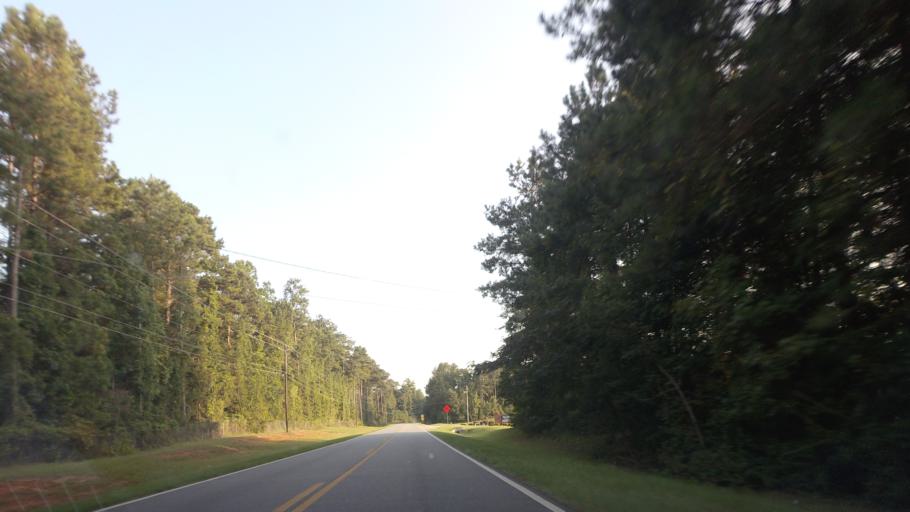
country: US
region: Georgia
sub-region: Bibb County
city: West Point
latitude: 32.8588
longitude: -83.7841
